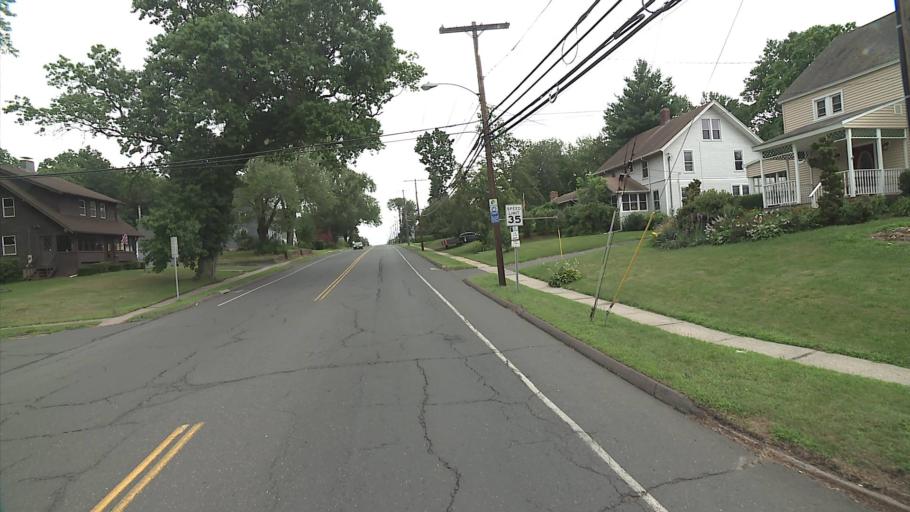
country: US
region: Connecticut
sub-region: Hartford County
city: Wethersfield
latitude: 41.7224
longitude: -72.6774
